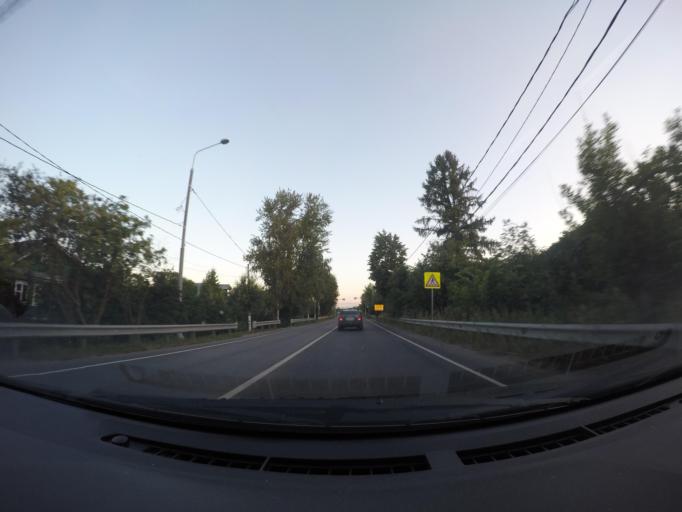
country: RU
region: Moskovskaya
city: Gzhel'
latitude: 55.6227
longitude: 38.3759
